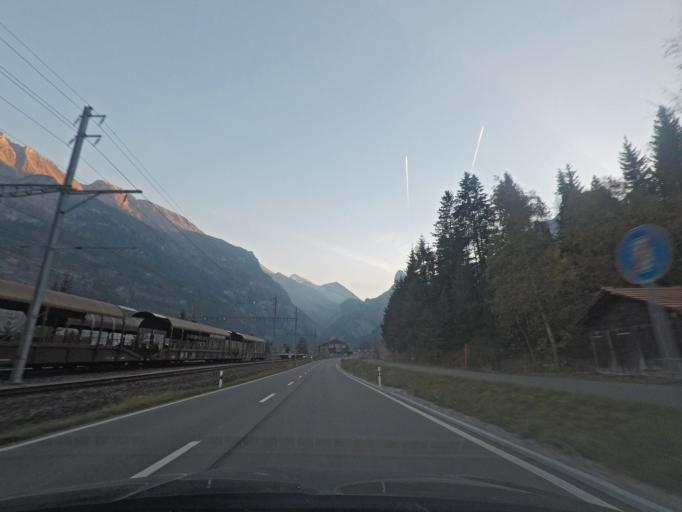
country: CH
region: Bern
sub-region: Frutigen-Niedersimmental District
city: Kandersteg
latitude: 46.5007
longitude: 7.6731
